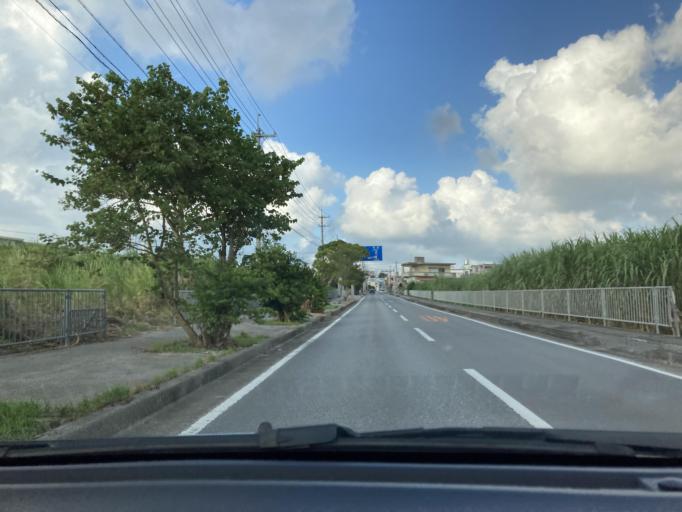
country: JP
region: Okinawa
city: Itoman
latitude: 26.1476
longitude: 127.7063
